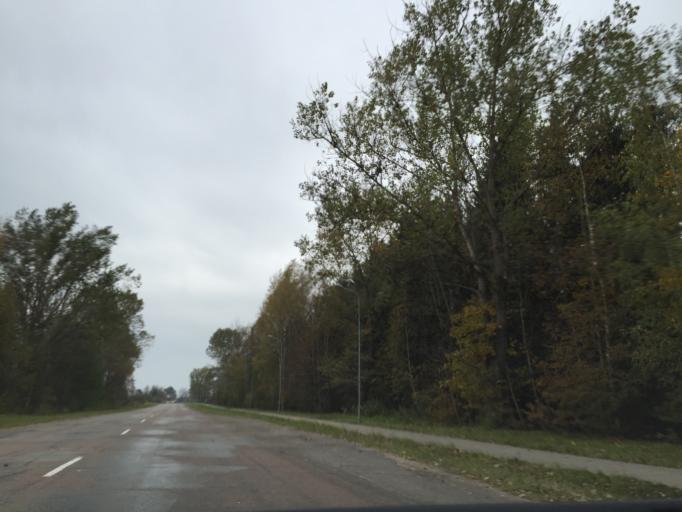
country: LV
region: Marupe
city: Marupe
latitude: 56.8494
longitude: 24.0505
